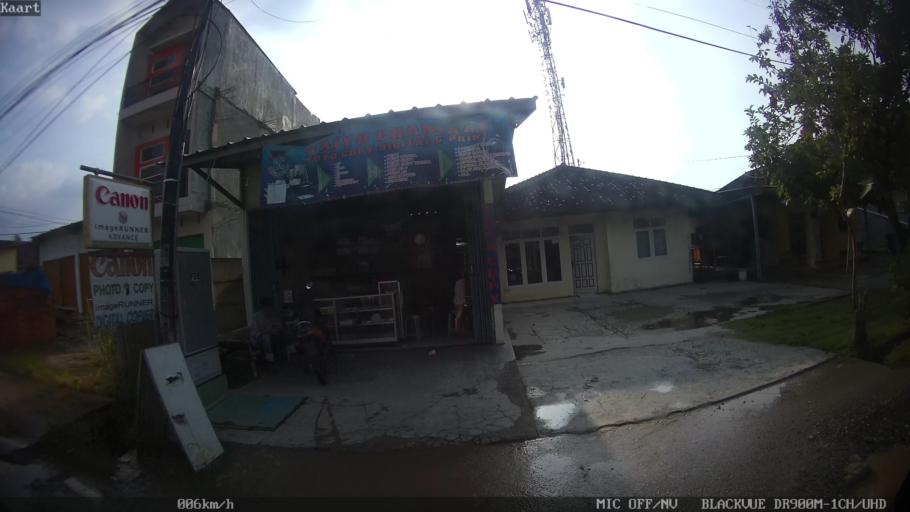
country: ID
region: Lampung
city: Kedaton
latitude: -5.3905
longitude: 105.3155
